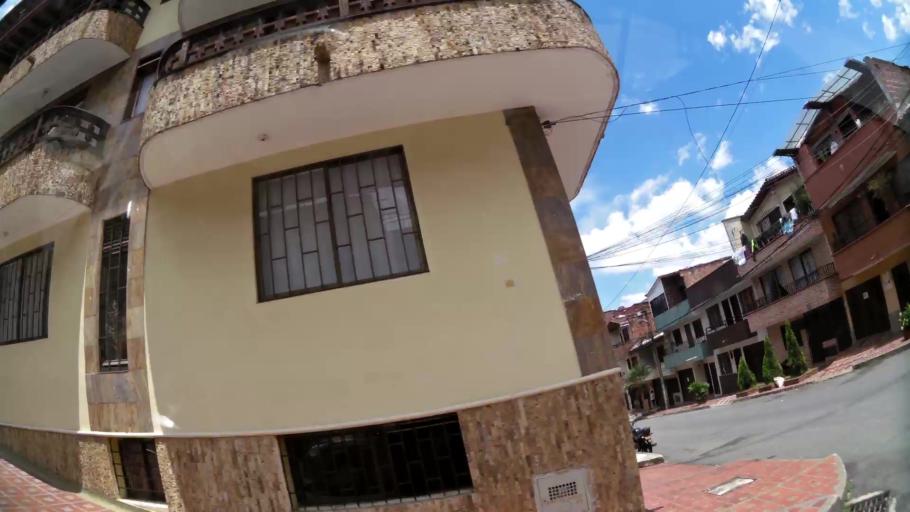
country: CO
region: Antioquia
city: La Estrella
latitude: 6.1605
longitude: -75.6395
